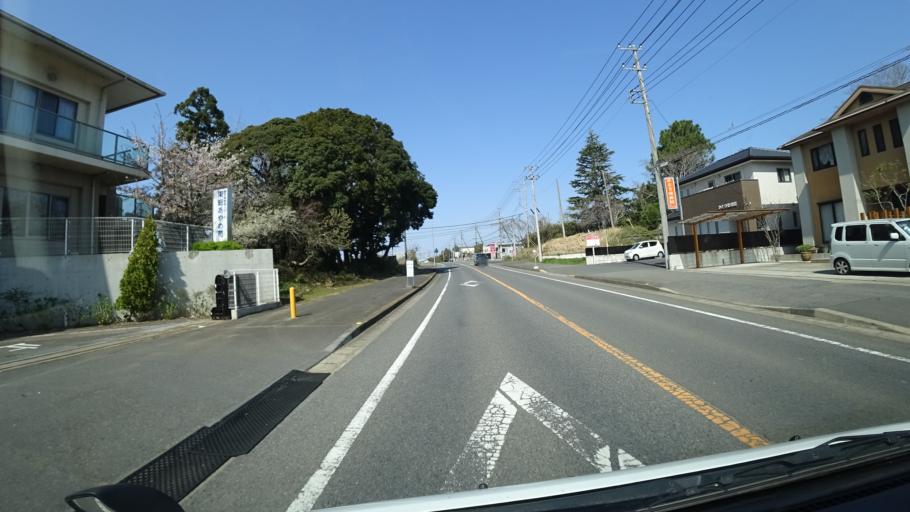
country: JP
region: Chiba
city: Sawara
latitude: 35.8829
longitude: 140.4861
